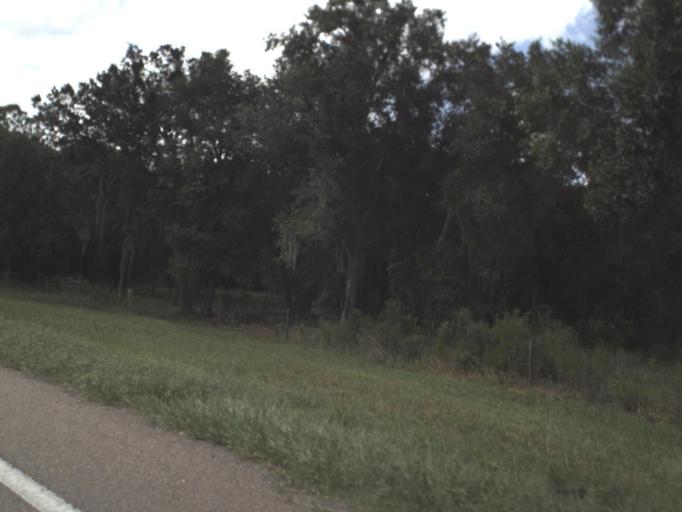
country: US
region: Florida
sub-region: Hardee County
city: Wauchula
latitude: 27.4856
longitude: -81.9407
